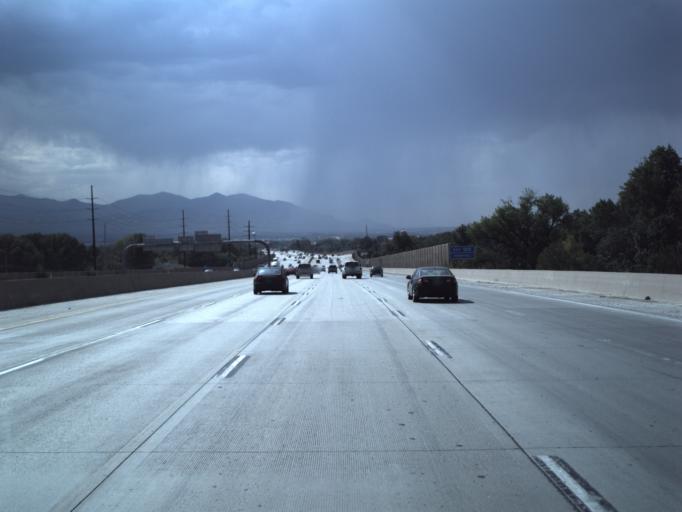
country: US
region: Utah
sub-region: Salt Lake County
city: Willard
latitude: 40.7198
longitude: -111.8583
